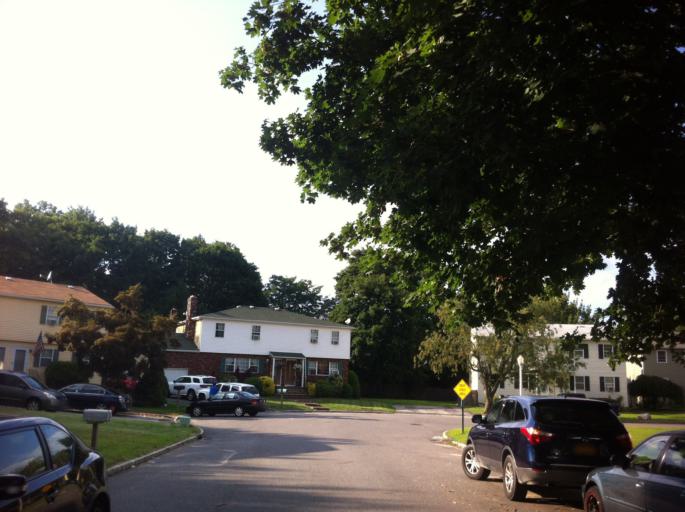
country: US
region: New York
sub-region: Nassau County
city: Glen Cove
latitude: 40.8512
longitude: -73.6329
